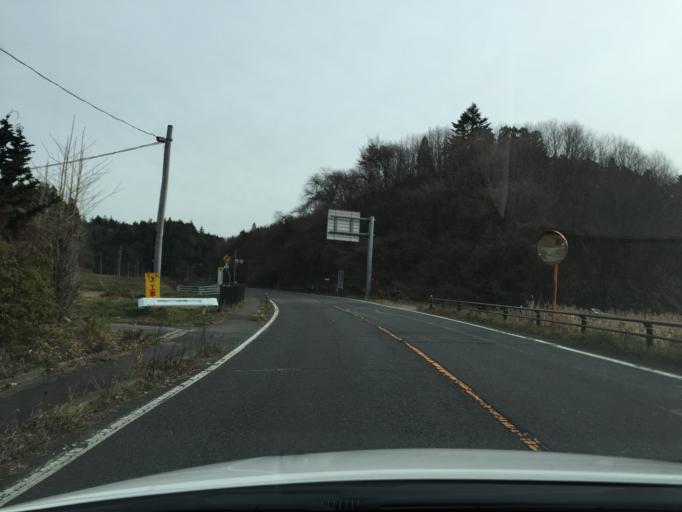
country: JP
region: Fukushima
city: Ishikawa
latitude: 37.2215
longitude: 140.5855
